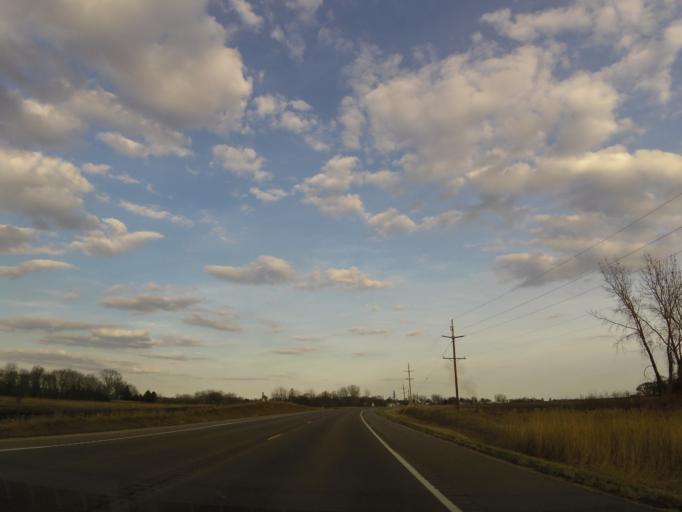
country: US
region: Minnesota
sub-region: McLeod County
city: Hutchinson
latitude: 44.7235
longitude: -94.5037
